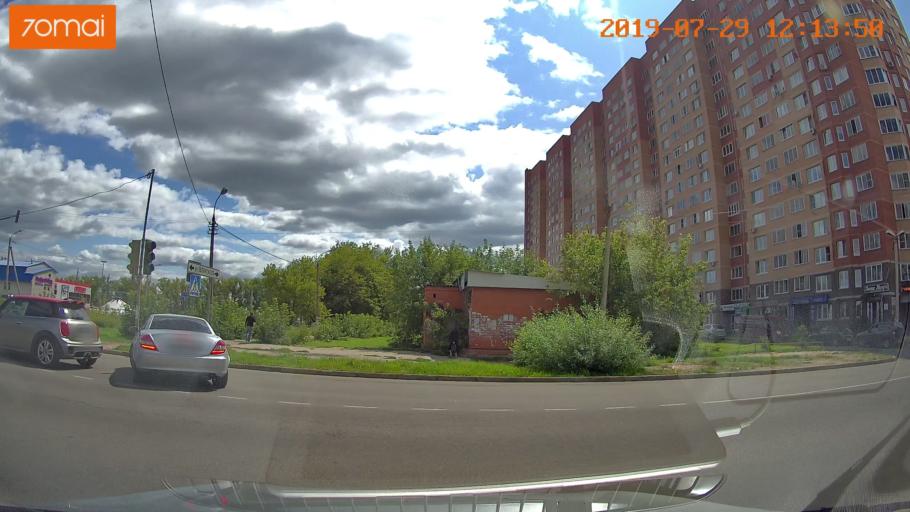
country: RU
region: Moskovskaya
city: Voskresensk
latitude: 55.3131
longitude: 38.6534
